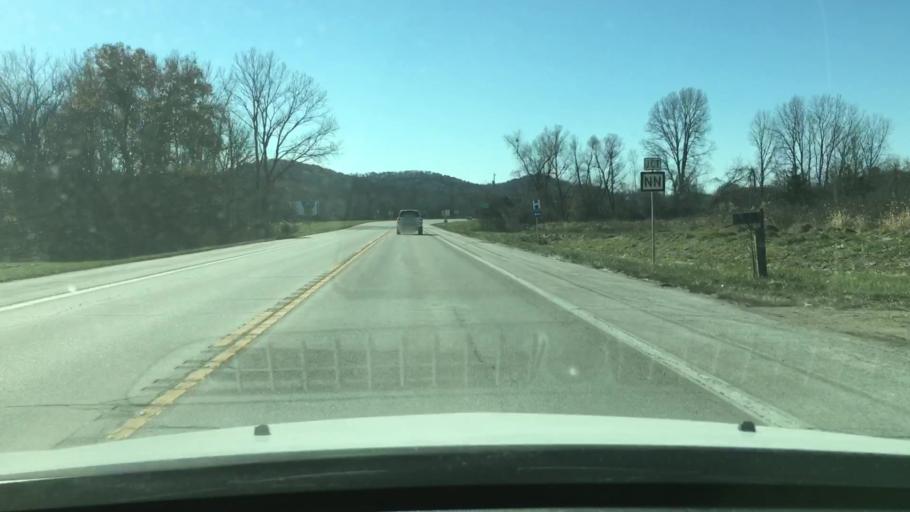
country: US
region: Missouri
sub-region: Pike County
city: Louisiana
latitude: 39.4232
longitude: -91.0859
